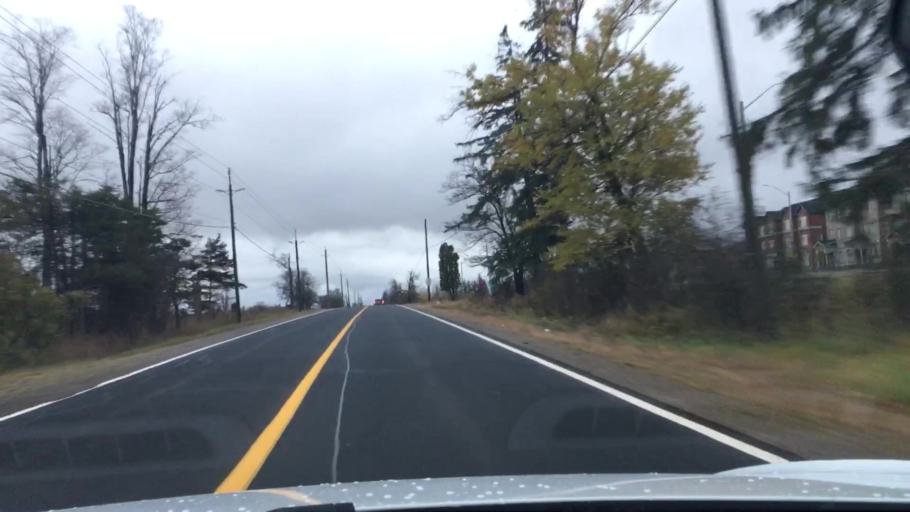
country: CA
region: Ontario
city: Markham
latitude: 43.8948
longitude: -79.2131
